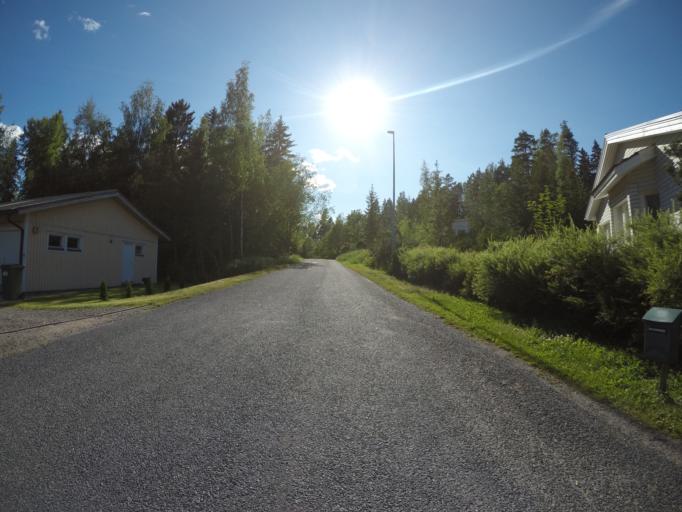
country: FI
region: Haeme
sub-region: Haemeenlinna
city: Haemeenlinna
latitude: 61.0198
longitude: 24.5091
